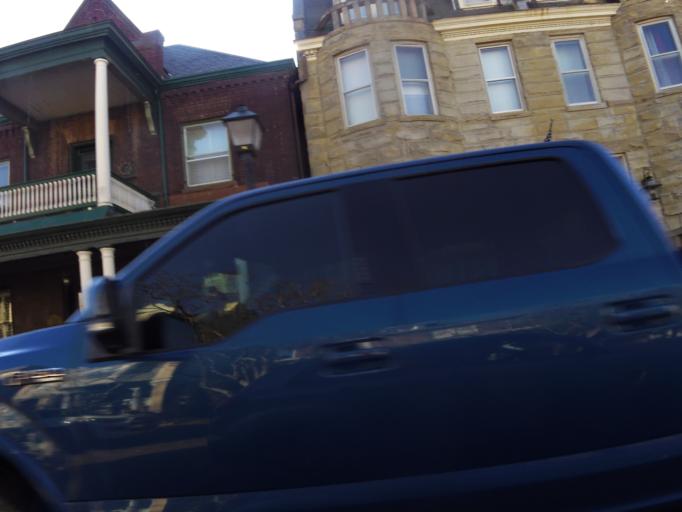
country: US
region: Virginia
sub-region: City of Portsmouth
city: Portsmouth
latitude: 36.8383
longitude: -76.3017
